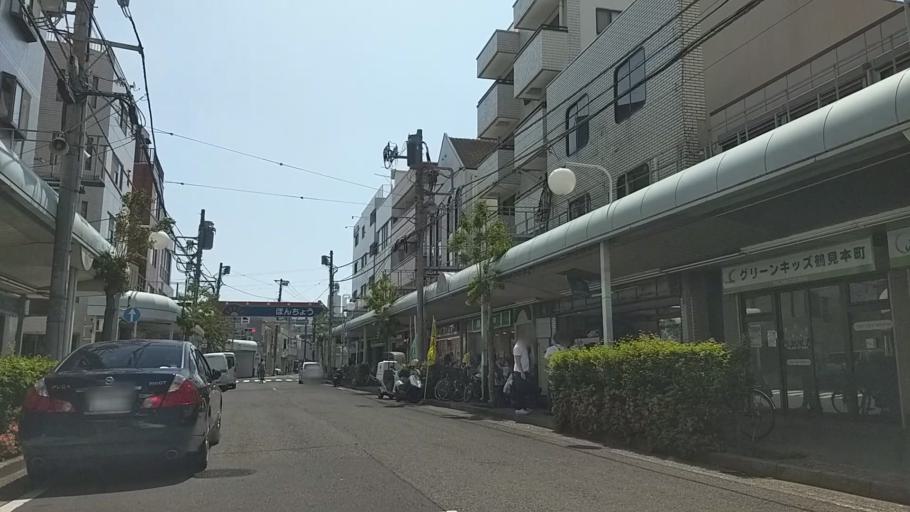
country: JP
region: Kanagawa
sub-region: Kawasaki-shi
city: Kawasaki
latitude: 35.5015
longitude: 139.6839
